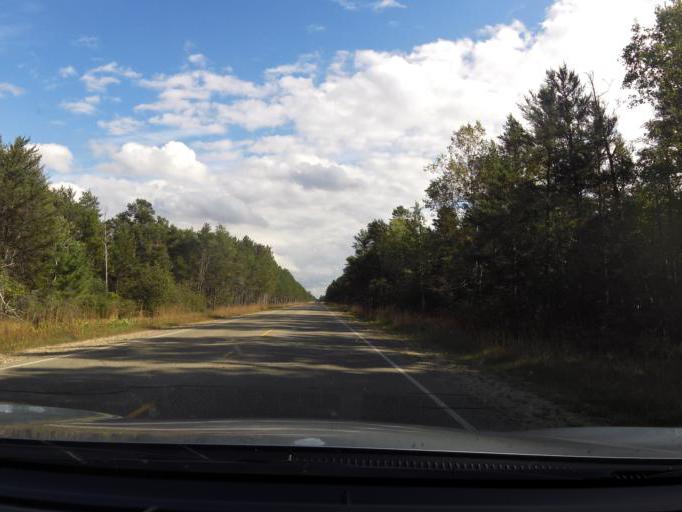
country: US
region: Michigan
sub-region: Roscommon County
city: Roscommon
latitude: 44.4815
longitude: -84.5637
